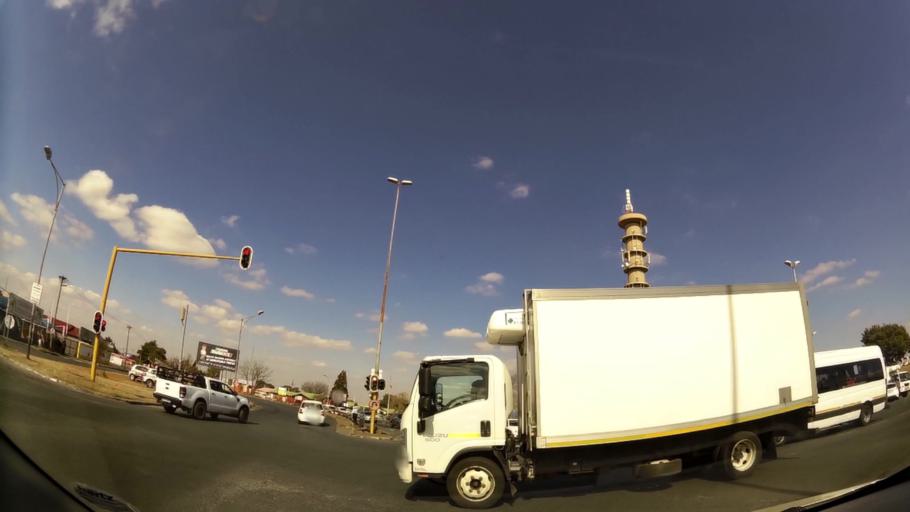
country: ZA
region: Gauteng
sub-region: West Rand District Municipality
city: Krugersdorp
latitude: -26.1198
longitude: 27.8181
